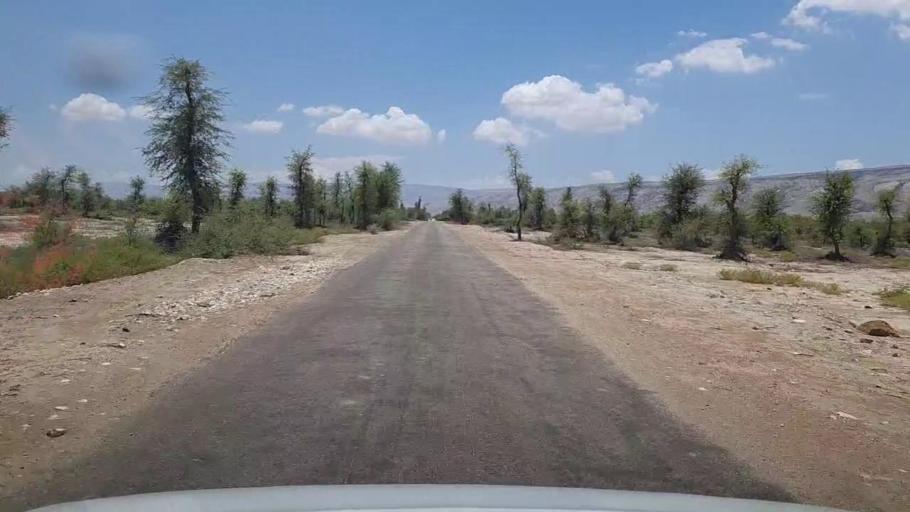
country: PK
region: Sindh
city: Bhan
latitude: 26.2809
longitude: 67.5296
